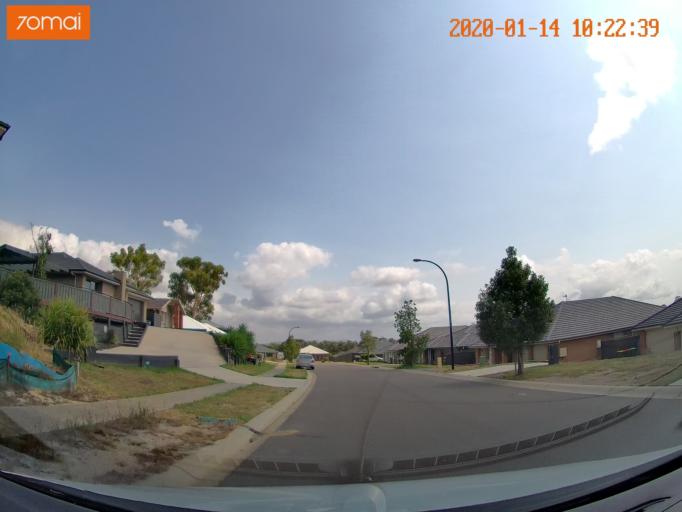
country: AU
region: New South Wales
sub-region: Lake Macquarie Shire
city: Dora Creek
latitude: -33.1108
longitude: 151.5105
